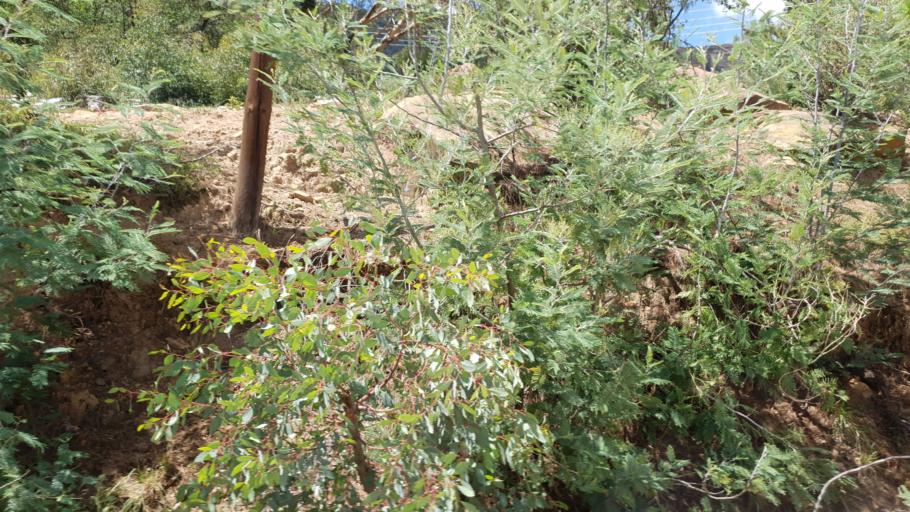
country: LS
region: Maseru
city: Nako
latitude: -29.6308
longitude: 27.5090
